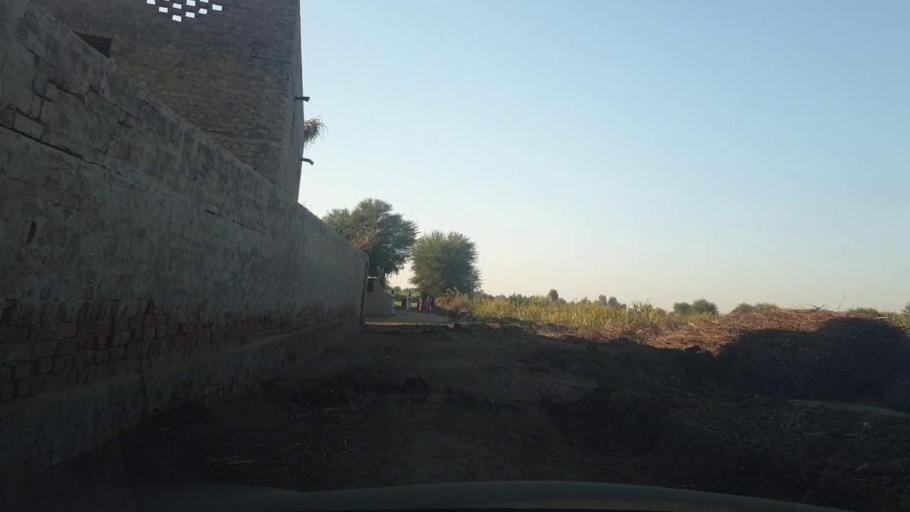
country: PK
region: Sindh
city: Ghotki
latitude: 28.0967
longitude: 69.3619
